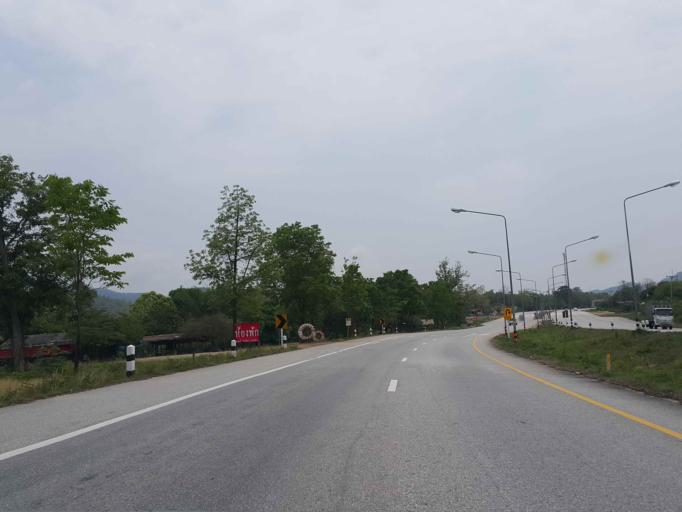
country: TH
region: Lampang
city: Thoen
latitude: 17.7381
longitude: 99.2337
